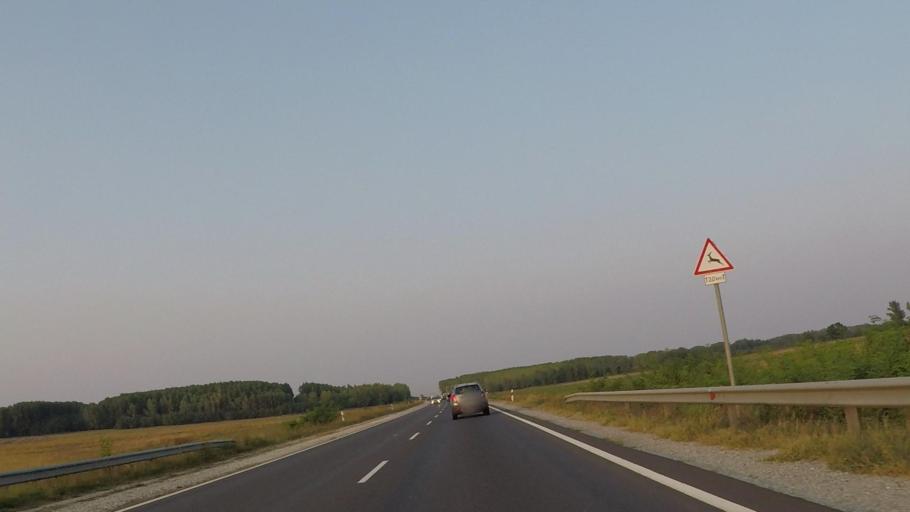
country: HU
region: Pest
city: Abony
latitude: 47.2025
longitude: 19.9543
